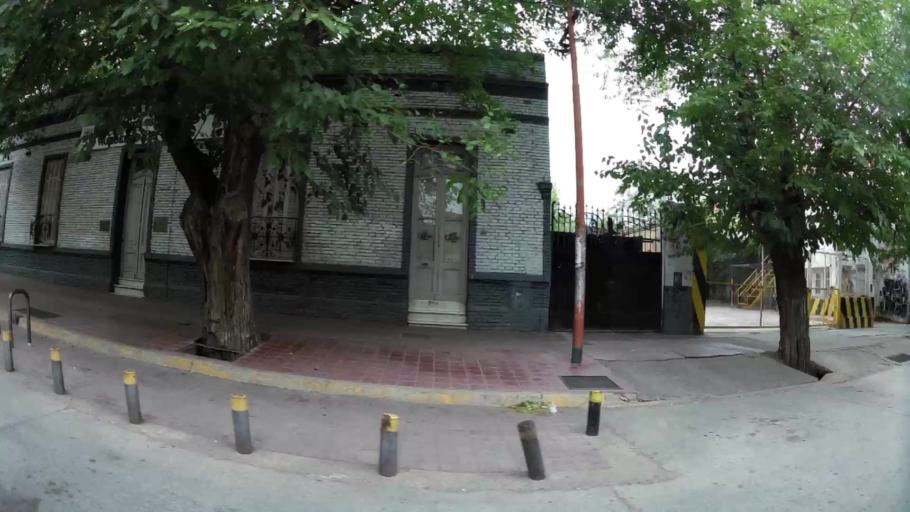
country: AR
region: Mendoza
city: Mendoza
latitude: -32.8951
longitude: -68.8460
